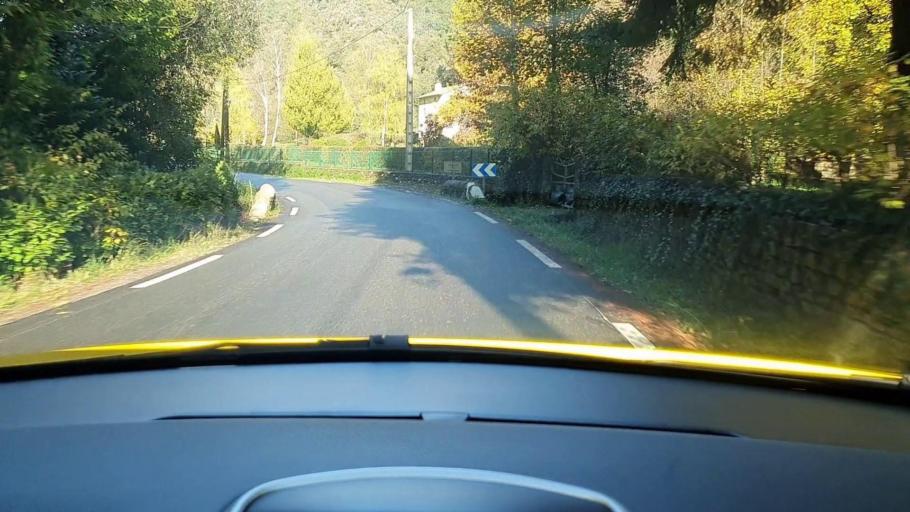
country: FR
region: Languedoc-Roussillon
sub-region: Departement du Gard
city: Lasalle
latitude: 44.1281
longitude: 3.7628
